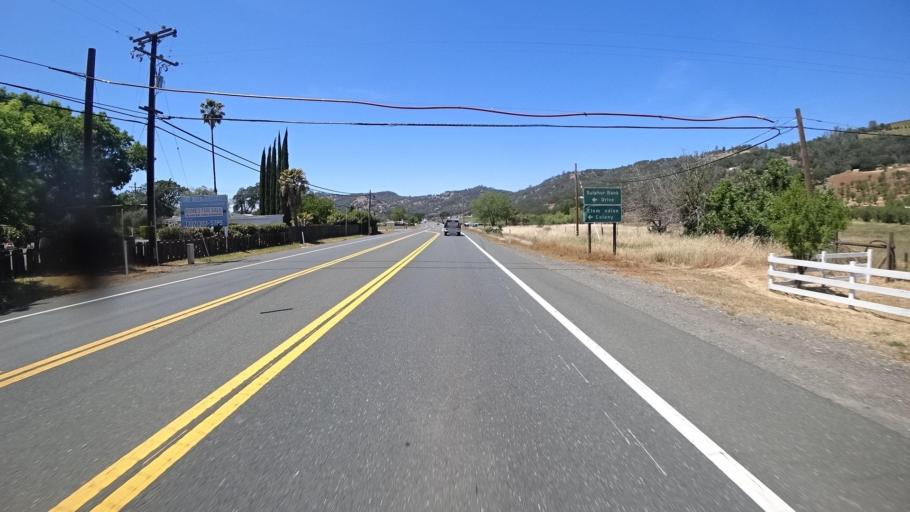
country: US
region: California
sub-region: Lake County
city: Clearlake Oaks
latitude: 39.0196
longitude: -122.6474
